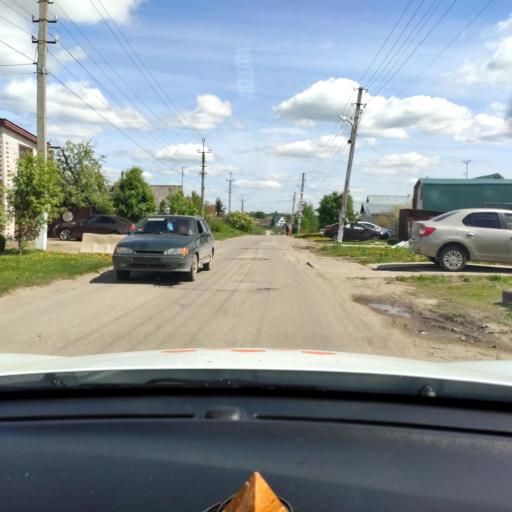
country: RU
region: Tatarstan
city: Osinovo
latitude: 55.8817
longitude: 48.8718
